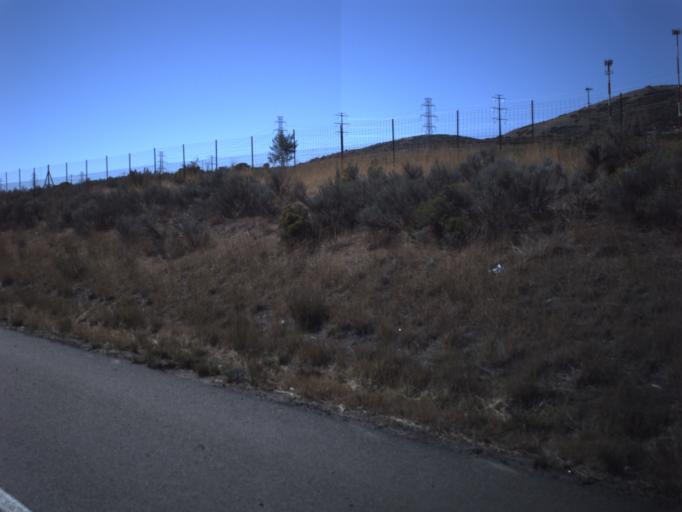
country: US
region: Utah
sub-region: Salt Lake County
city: Bluffdale
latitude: 40.4564
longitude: -111.9400
